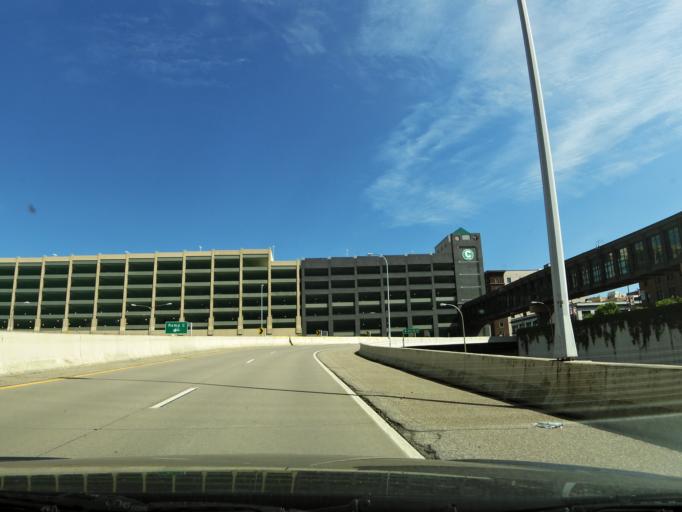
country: US
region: Minnesota
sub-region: Hennepin County
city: Minneapolis
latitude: 44.9817
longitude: -93.2753
